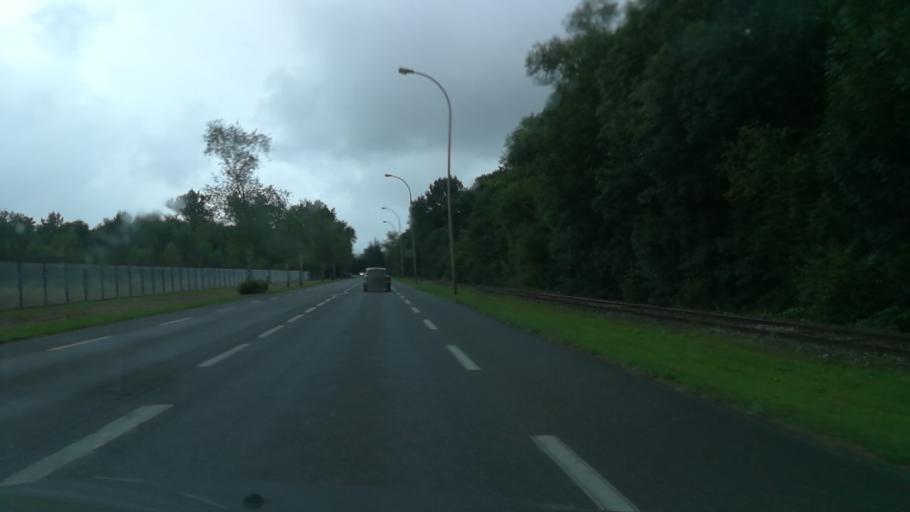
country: FR
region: Aquitaine
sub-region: Departement des Pyrenees-Atlantiques
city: Mourenx
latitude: 43.3878
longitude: -0.5826
